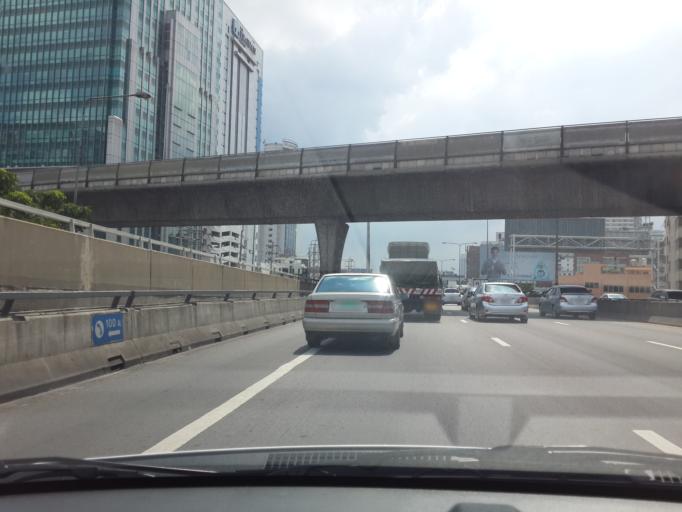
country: TH
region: Bangkok
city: Ratchathewi
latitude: 13.7430
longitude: 100.5505
